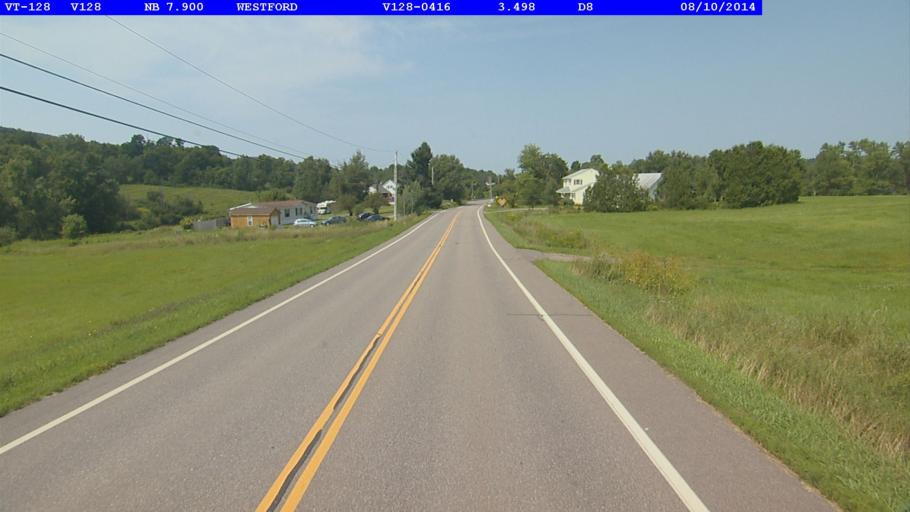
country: US
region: Vermont
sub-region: Chittenden County
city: Jericho
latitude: 44.6075
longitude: -73.0090
